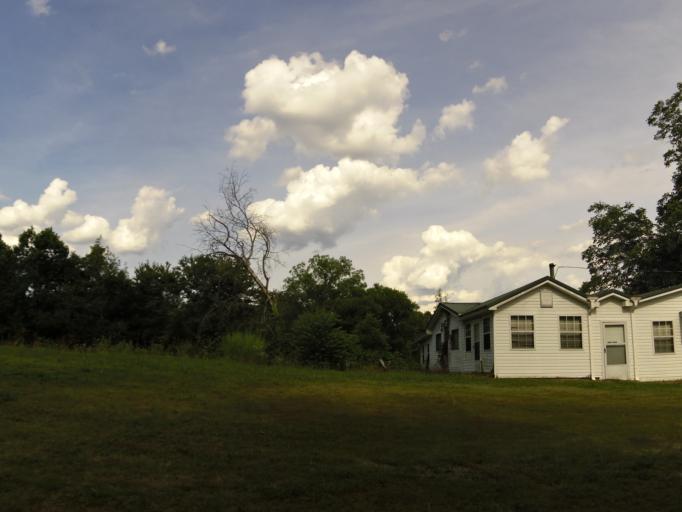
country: US
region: Tennessee
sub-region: Benton County
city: Camden
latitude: 36.0478
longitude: -88.1679
